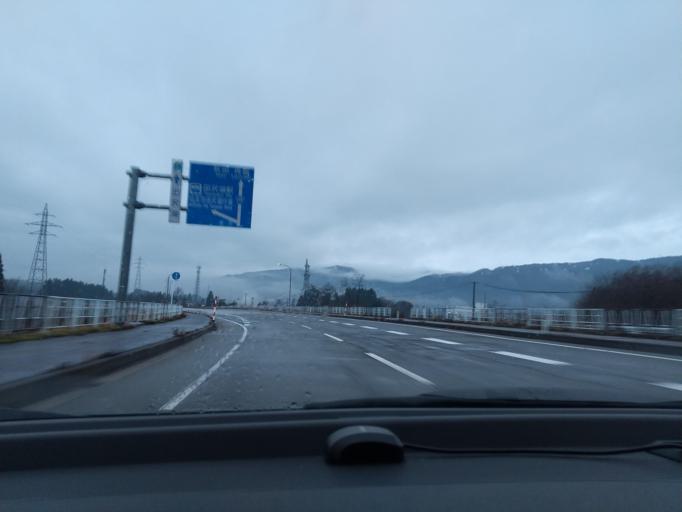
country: JP
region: Akita
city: Kakunodatemachi
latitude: 39.7007
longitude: 140.7346
